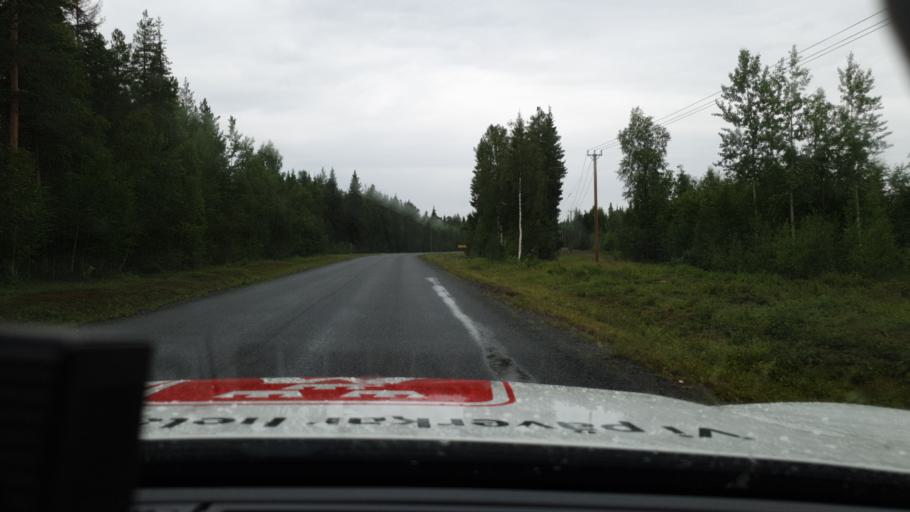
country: SE
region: Norrbotten
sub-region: Bodens Kommun
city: Boden
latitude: 65.9798
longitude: 21.8473
